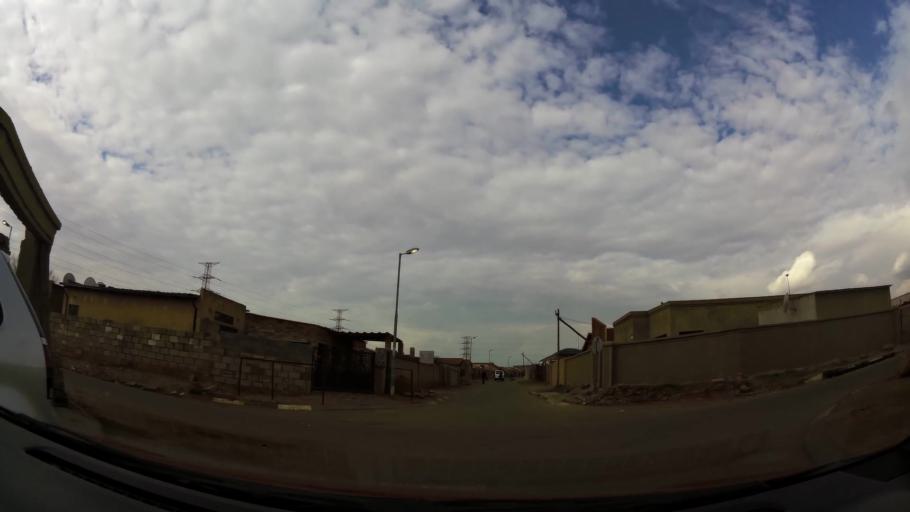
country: ZA
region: Gauteng
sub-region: City of Johannesburg Metropolitan Municipality
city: Soweto
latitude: -26.2417
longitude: 27.8537
